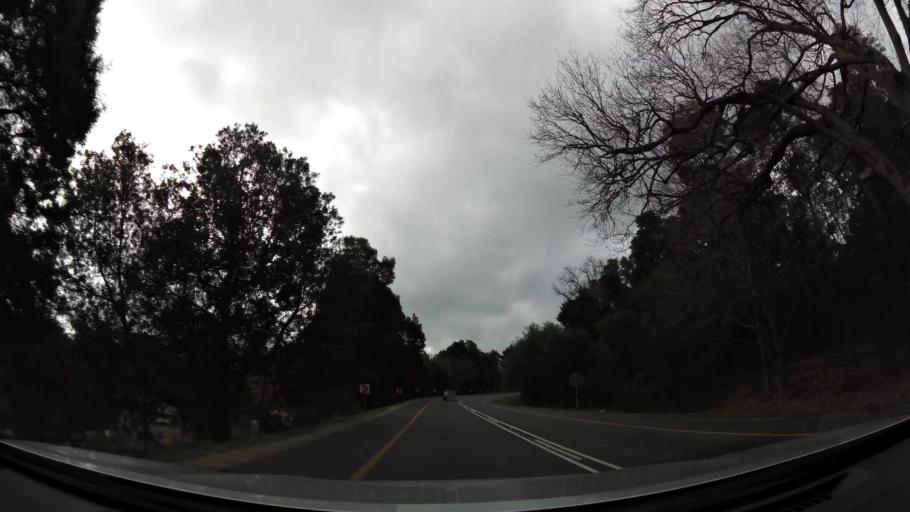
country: ZA
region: Western Cape
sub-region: Eden District Municipality
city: Knysna
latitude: -34.0273
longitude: 23.1595
